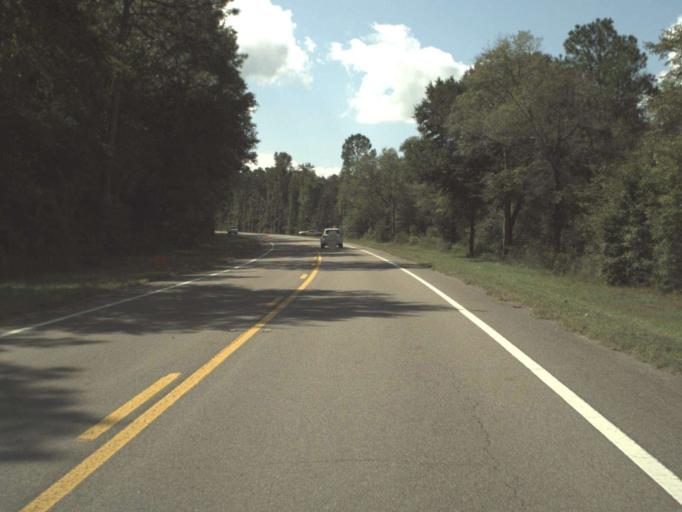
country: US
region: Florida
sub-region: Walton County
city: Freeport
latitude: 30.4792
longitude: -85.9598
